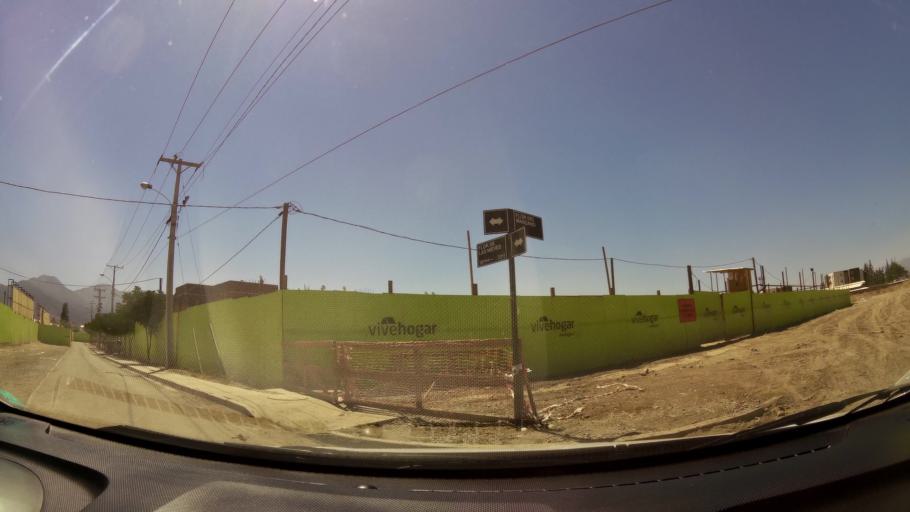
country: CL
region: O'Higgins
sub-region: Provincia de Cachapoal
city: Rancagua
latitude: -34.1733
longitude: -70.7793
